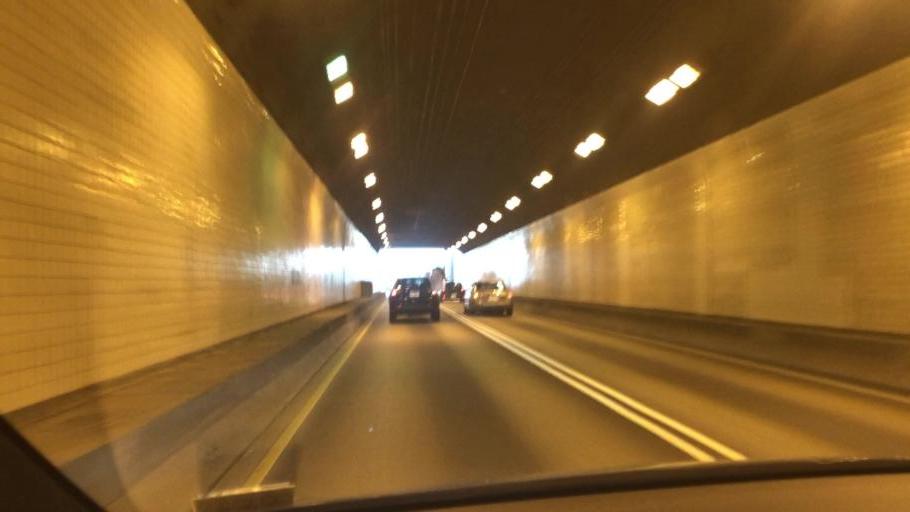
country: US
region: Pennsylvania
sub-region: Allegheny County
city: Homestead
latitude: 40.4286
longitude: -79.9176
